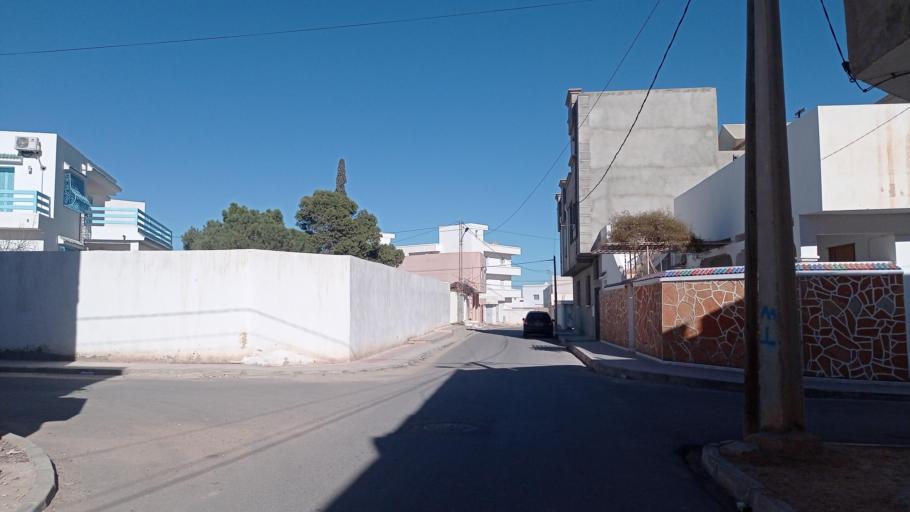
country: TN
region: Qabis
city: Gabes
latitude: 33.8469
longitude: 10.1111
